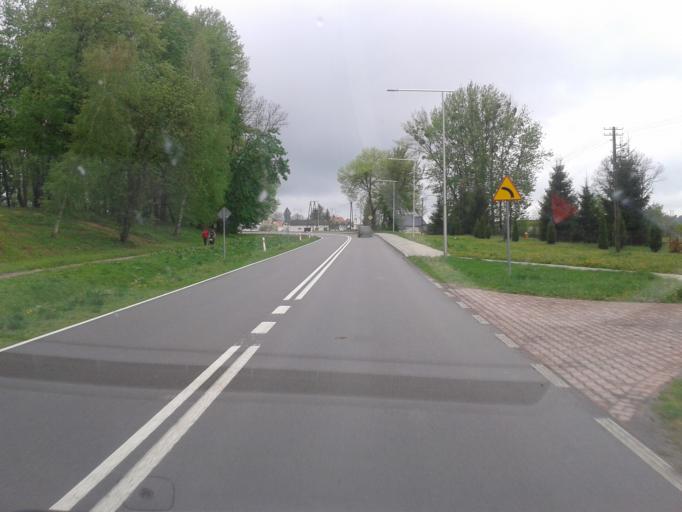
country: PL
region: Lublin Voivodeship
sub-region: Powiat hrubieszowski
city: Dolhobyczow
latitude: 50.5872
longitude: 24.0296
